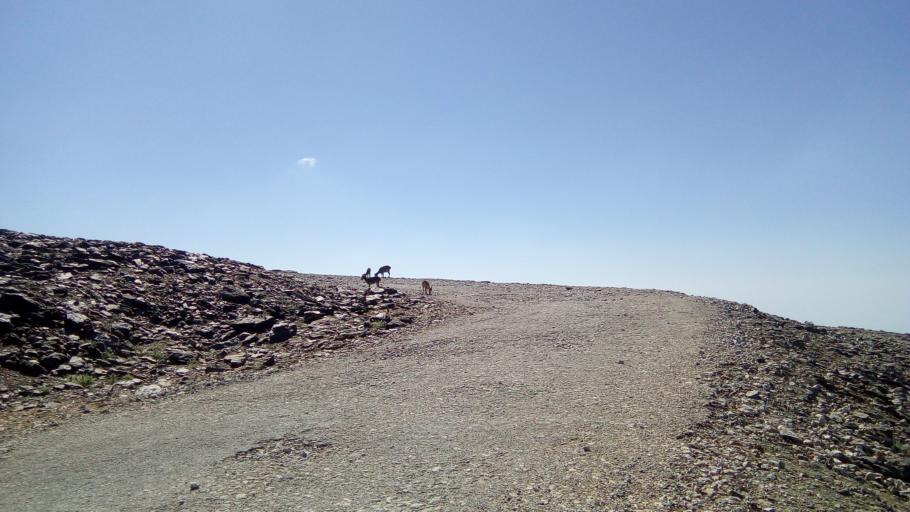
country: ES
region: Andalusia
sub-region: Provincia de Granada
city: Capileira
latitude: 37.0521
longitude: -3.3701
